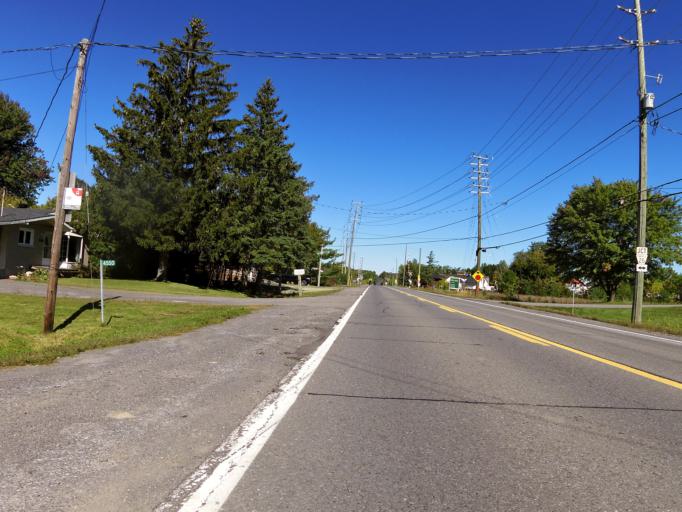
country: CA
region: Ontario
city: Clarence-Rockland
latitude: 45.3675
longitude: -75.4553
